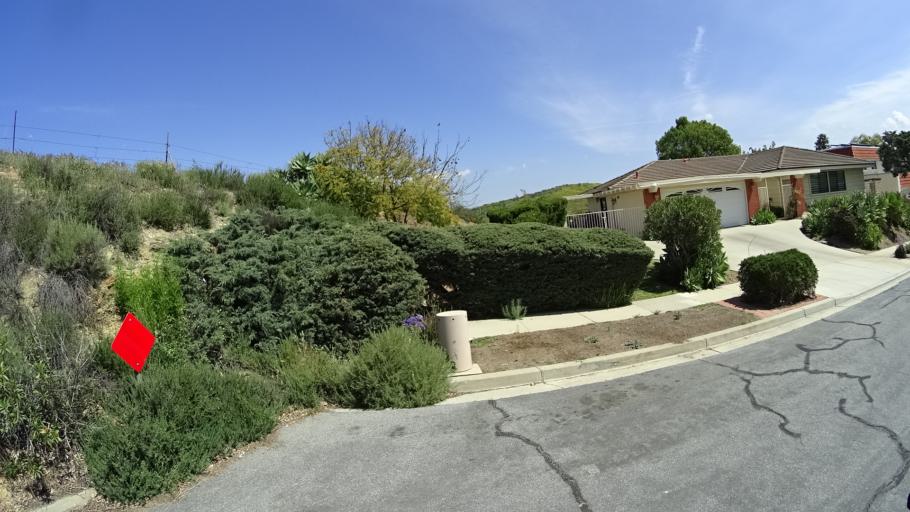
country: US
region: California
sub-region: Ventura County
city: Moorpark
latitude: 34.2396
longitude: -118.8539
